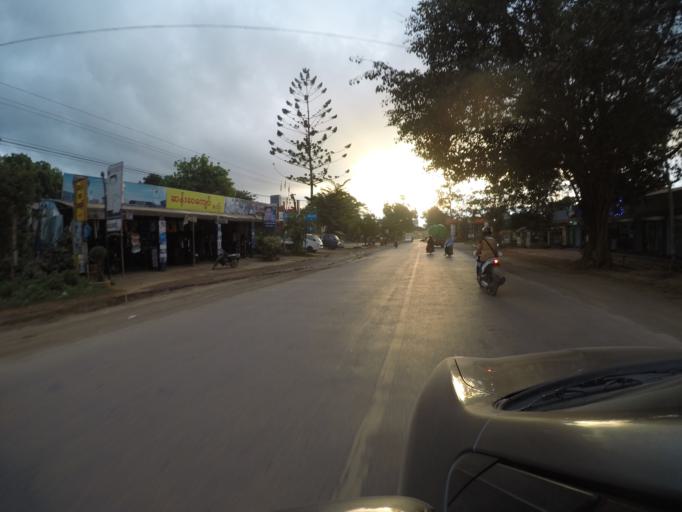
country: MM
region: Shan
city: Taunggyi
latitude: 20.7910
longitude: 97.0068
